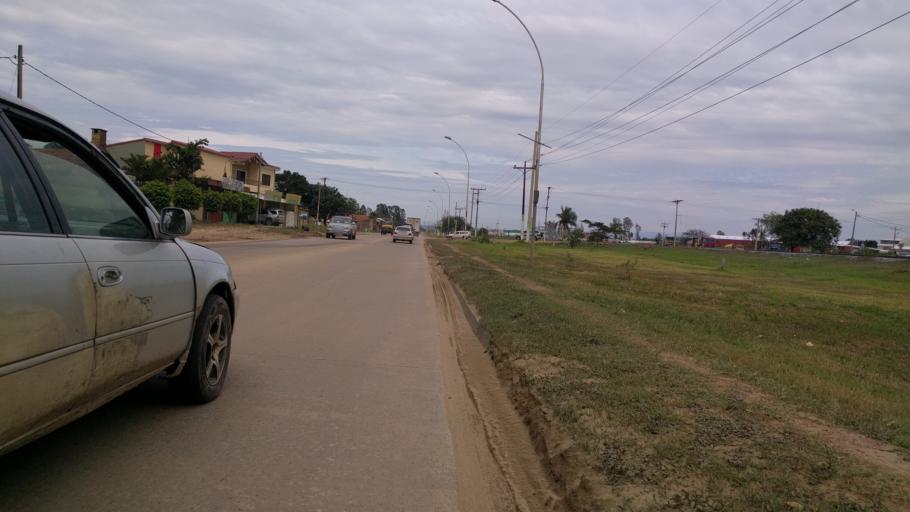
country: BO
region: Santa Cruz
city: Santa Cruz de la Sierra
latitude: -17.8455
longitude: -63.1752
